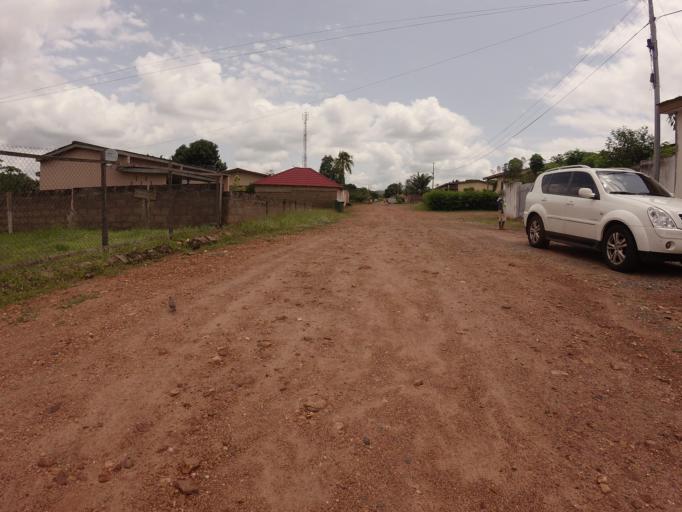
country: GH
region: Volta
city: Ho
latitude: 6.5897
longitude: 0.4767
